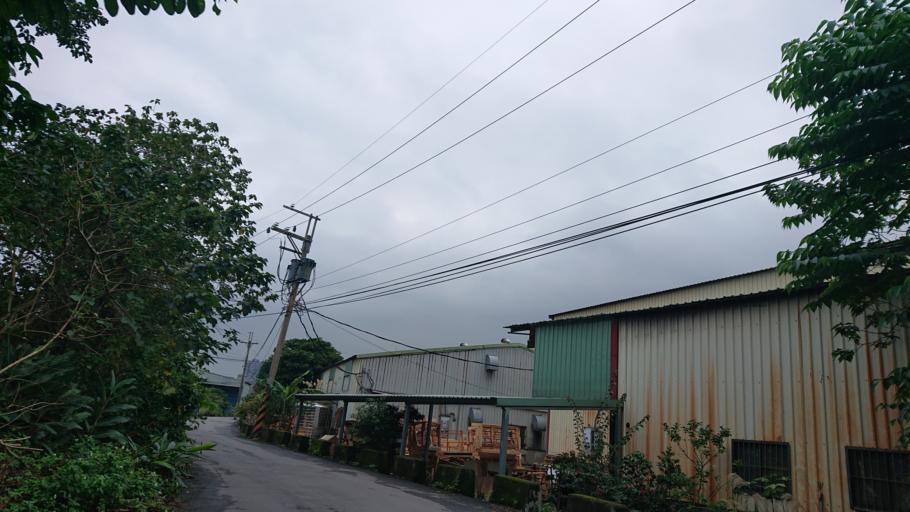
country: TW
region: Taiwan
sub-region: Taoyuan
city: Taoyuan
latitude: 24.9426
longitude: 121.3915
